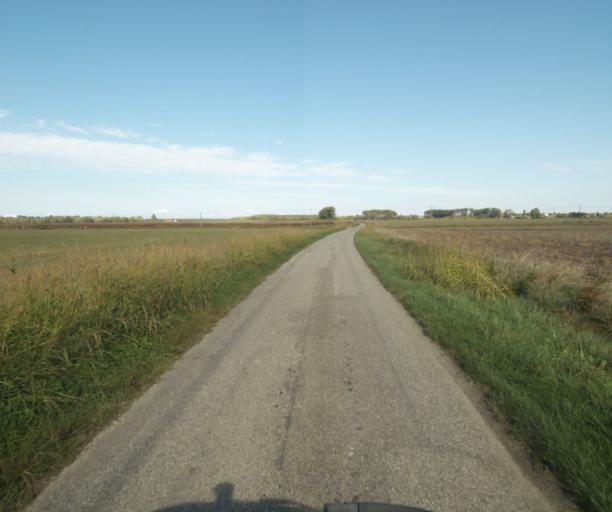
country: FR
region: Midi-Pyrenees
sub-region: Departement du Tarn-et-Garonne
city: Finhan
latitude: 43.8888
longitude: 1.2208
